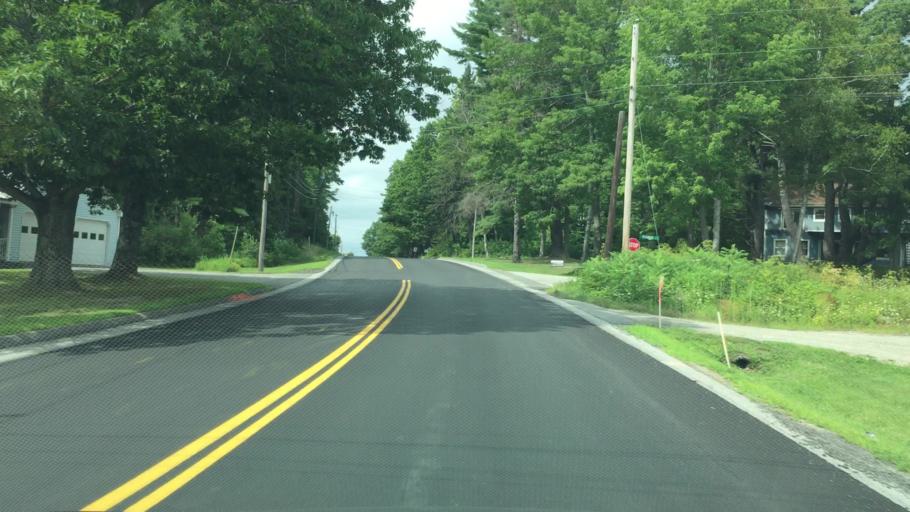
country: US
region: Maine
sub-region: Hancock County
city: Bucksport
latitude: 44.6037
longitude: -68.8170
